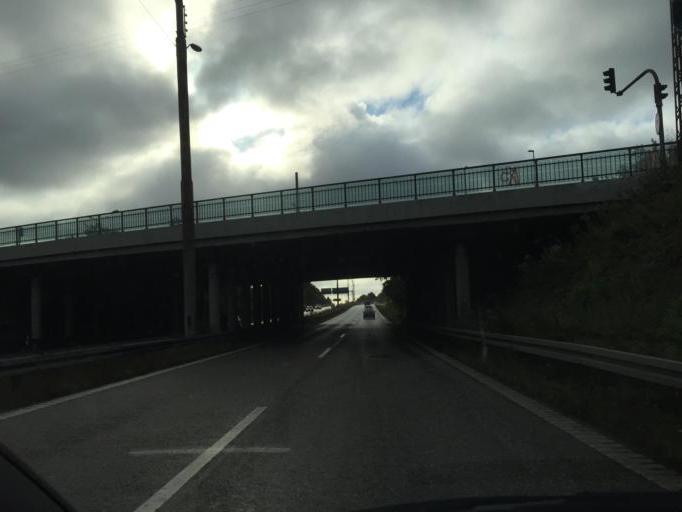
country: DK
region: Capital Region
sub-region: Herlev Kommune
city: Herlev
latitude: 55.7364
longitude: 12.4633
